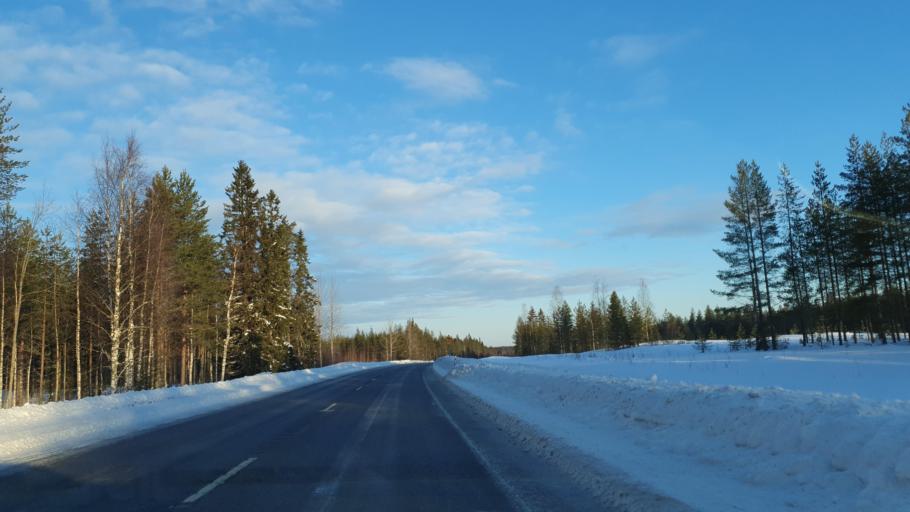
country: FI
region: Kainuu
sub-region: Kajaani
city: Vuolijoki
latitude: 64.5179
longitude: 27.2790
